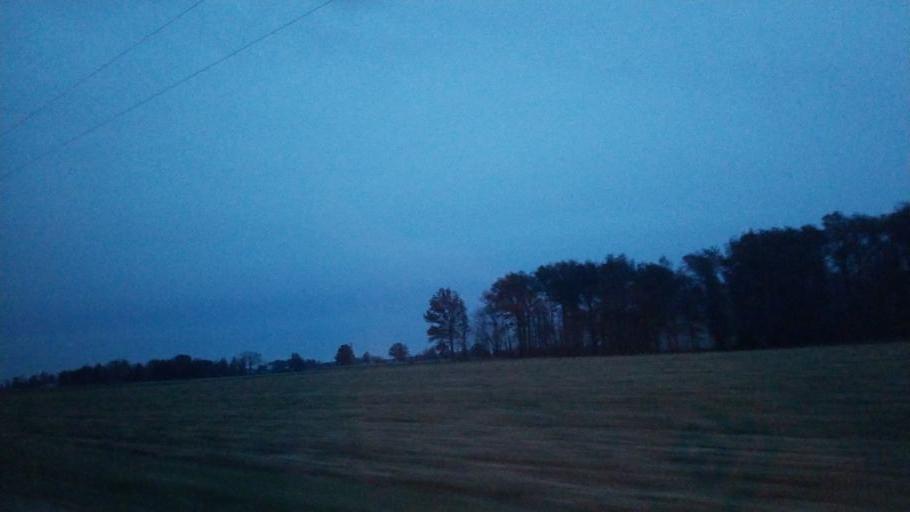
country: US
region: Indiana
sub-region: Adams County
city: Berne
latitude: 40.7068
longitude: -84.9940
